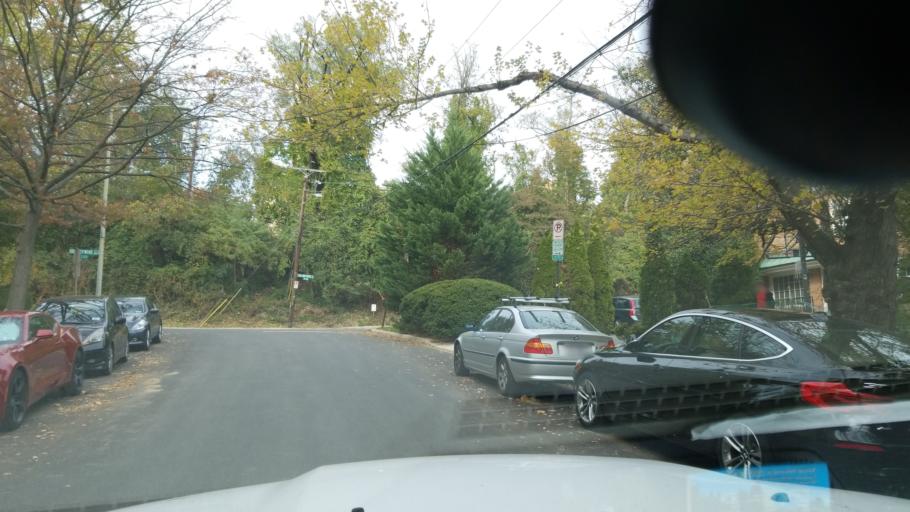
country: US
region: Maryland
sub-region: Montgomery County
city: Chevy Chase Village
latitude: 38.9493
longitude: -77.0643
